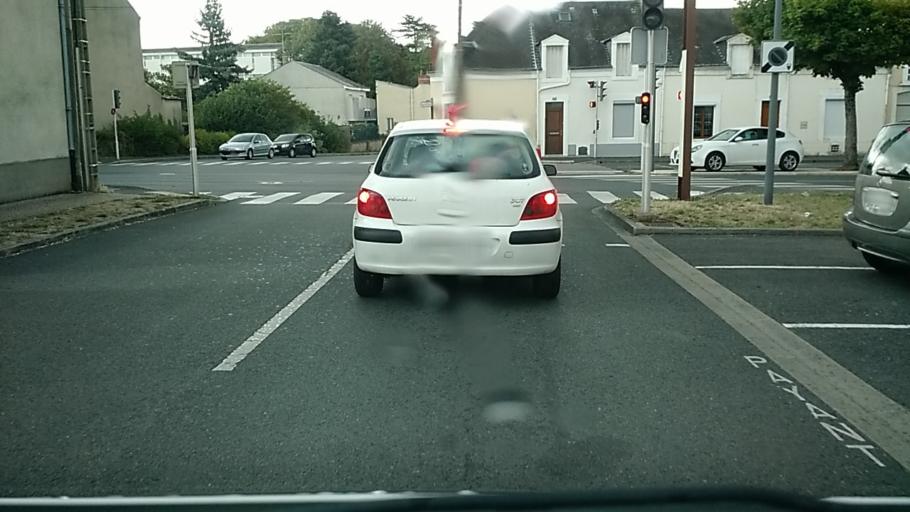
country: FR
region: Centre
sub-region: Departement de l'Indre
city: Chateauroux
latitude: 46.8105
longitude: 1.7054
